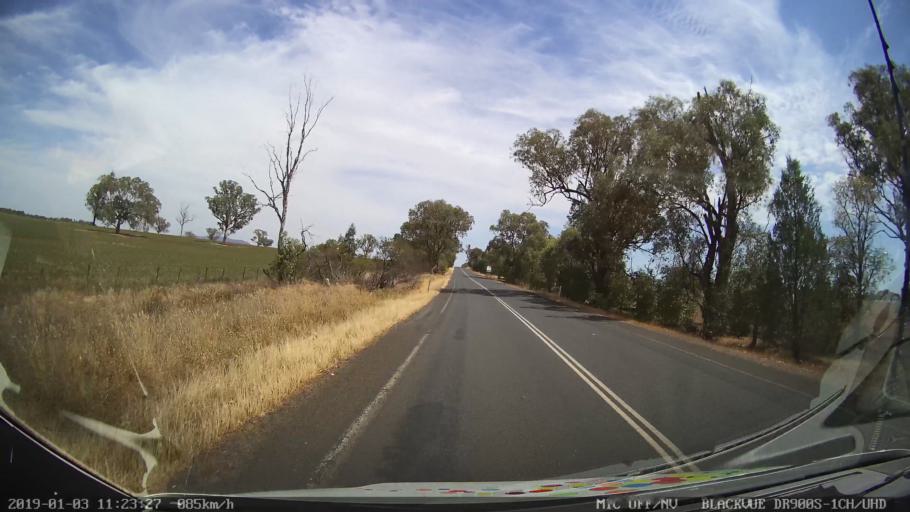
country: AU
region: New South Wales
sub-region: Weddin
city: Grenfell
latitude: -34.0630
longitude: 148.2427
